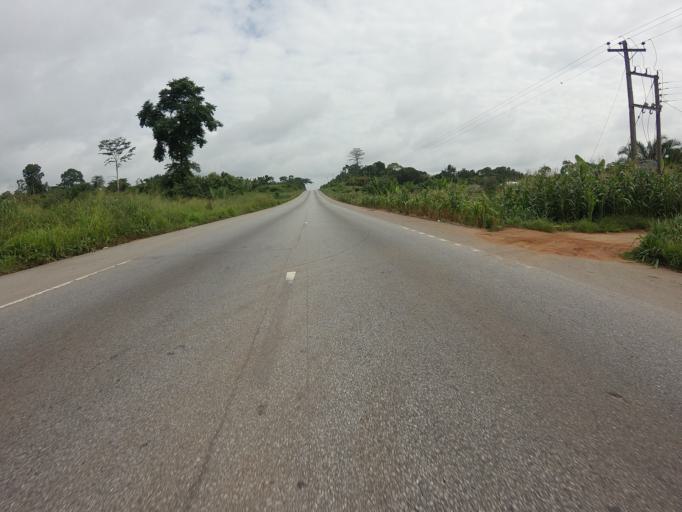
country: GH
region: Ashanti
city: Tafo
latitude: 6.9879
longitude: -1.6907
